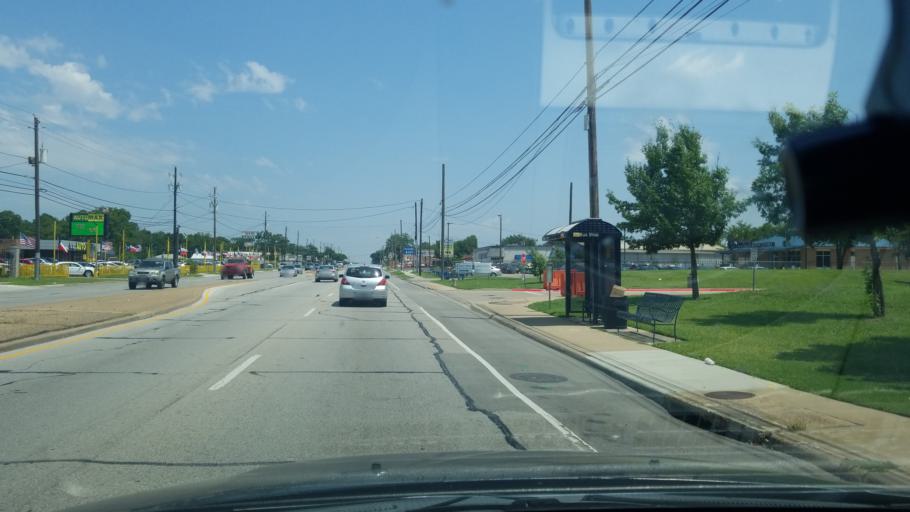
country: US
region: Texas
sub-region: Dallas County
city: Balch Springs
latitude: 32.7264
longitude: -96.6829
